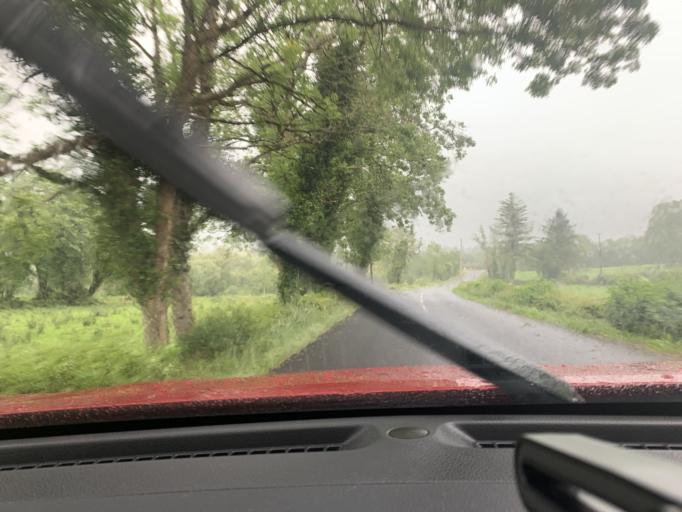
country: GB
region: Northern Ireland
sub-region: Fermanagh District
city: Enniskillen
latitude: 54.2934
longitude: -7.6969
